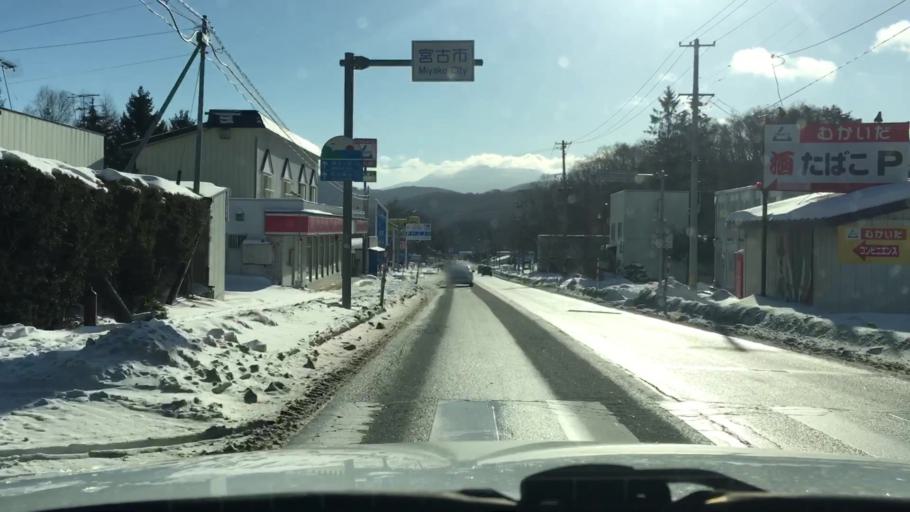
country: JP
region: Iwate
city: Morioka-shi
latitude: 39.6520
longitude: 141.3518
